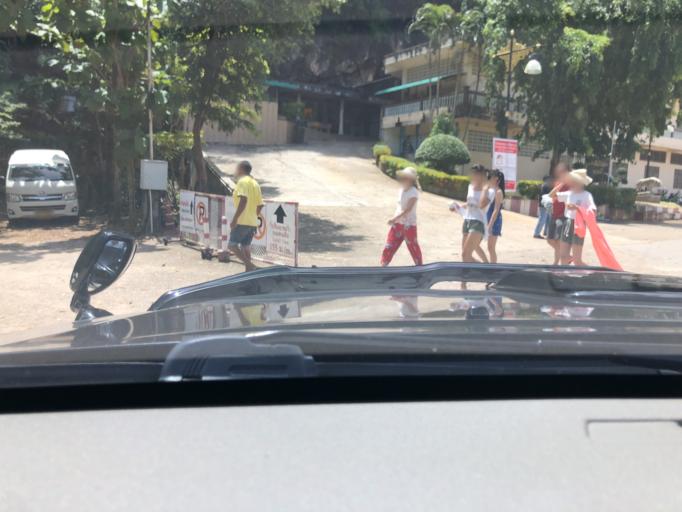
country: TH
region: Krabi
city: Krabi
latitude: 8.1238
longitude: 98.9245
